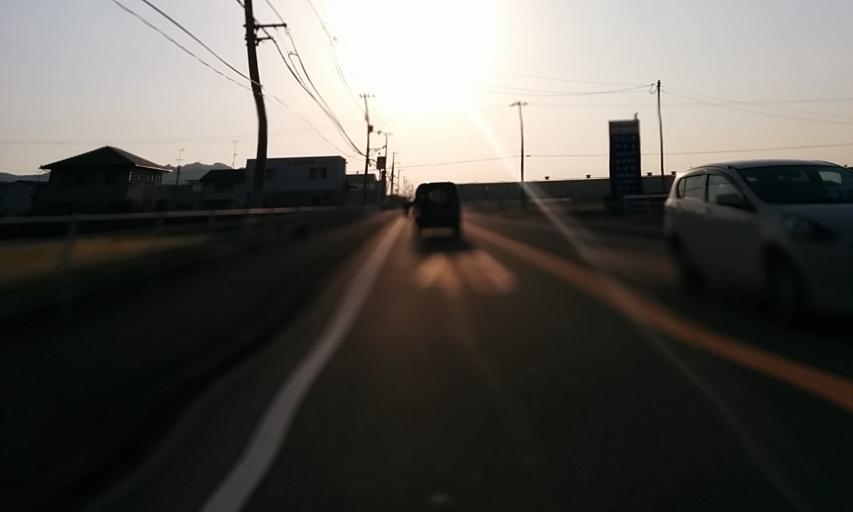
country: JP
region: Ehime
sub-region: Shikoku-chuo Shi
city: Matsuyama
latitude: 33.7819
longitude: 132.8092
